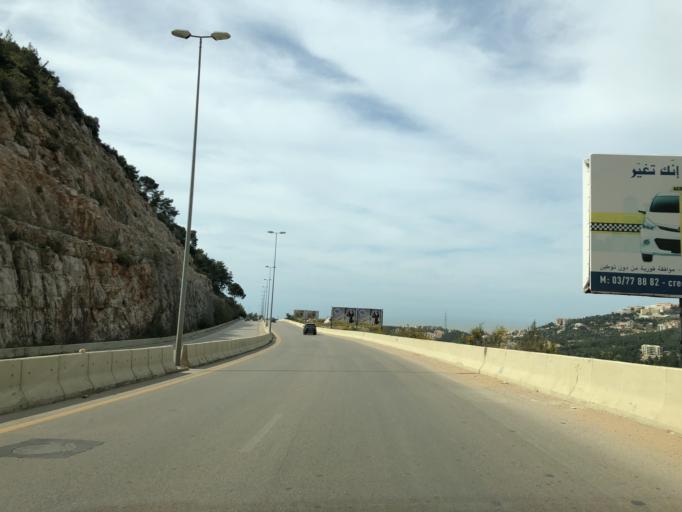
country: LB
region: Mont-Liban
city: Jdaidet el Matn
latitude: 33.8991
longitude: 35.6465
